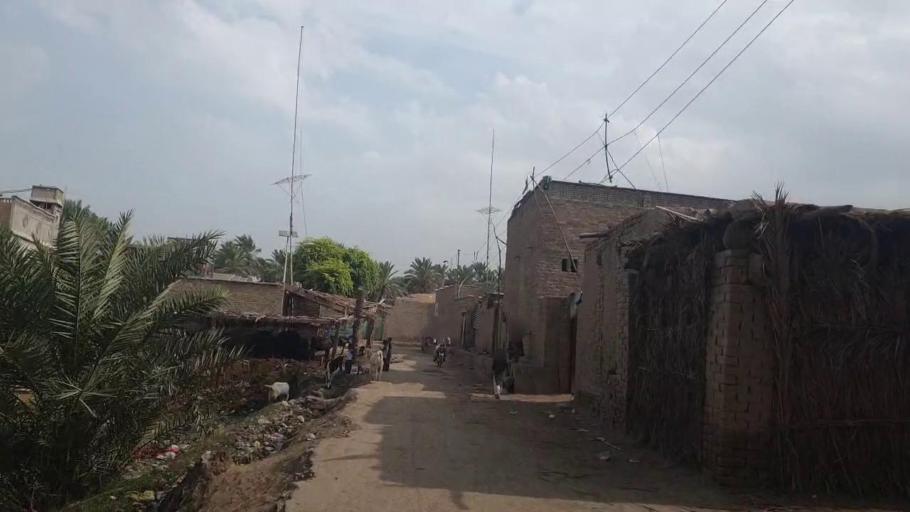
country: PK
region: Sindh
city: Sukkur
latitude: 27.6422
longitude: 68.8025
